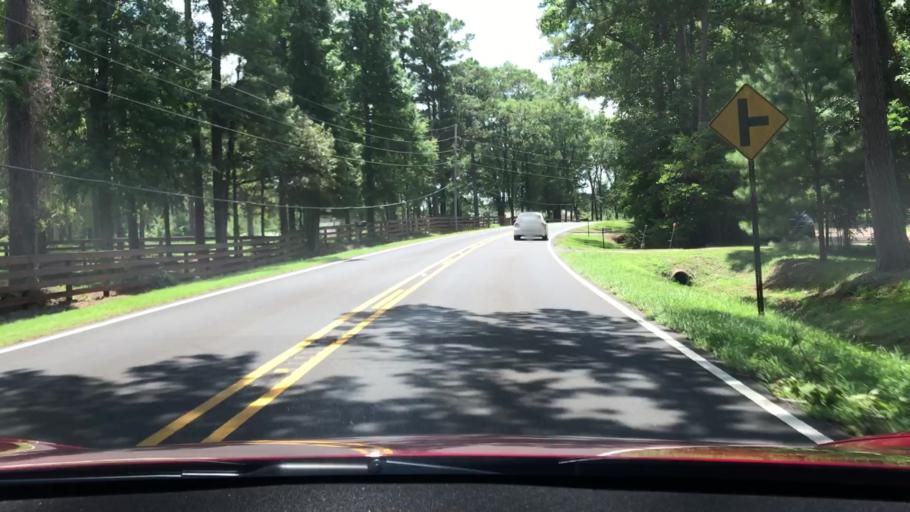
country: US
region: Louisiana
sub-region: Bossier Parish
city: Bossier City
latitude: 32.3657
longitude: -93.6879
